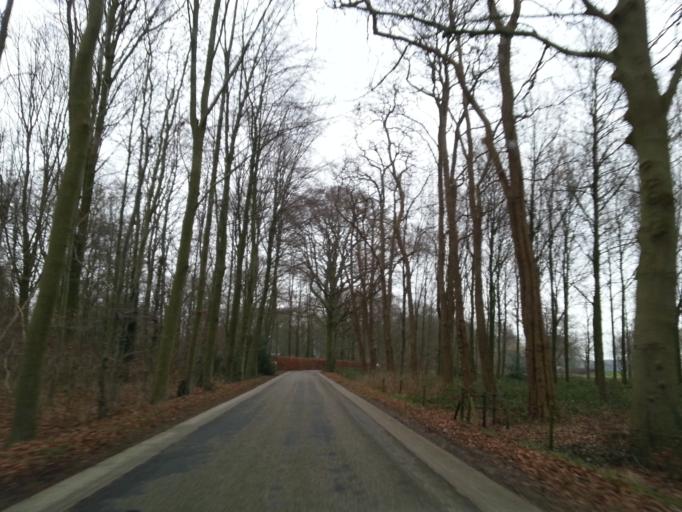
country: NL
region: Overijssel
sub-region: Gemeente Dalfsen
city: Dalfsen
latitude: 52.5087
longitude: 6.2426
